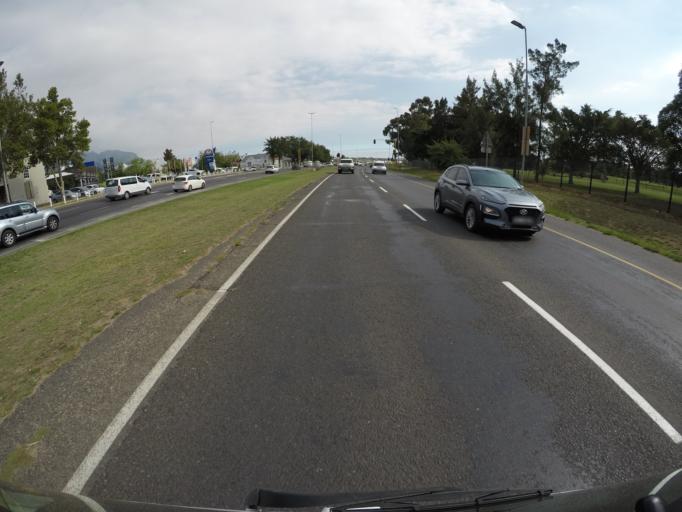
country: ZA
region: Western Cape
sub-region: Cape Winelands District Municipality
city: Stellenbosch
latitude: -33.9624
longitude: 18.8510
